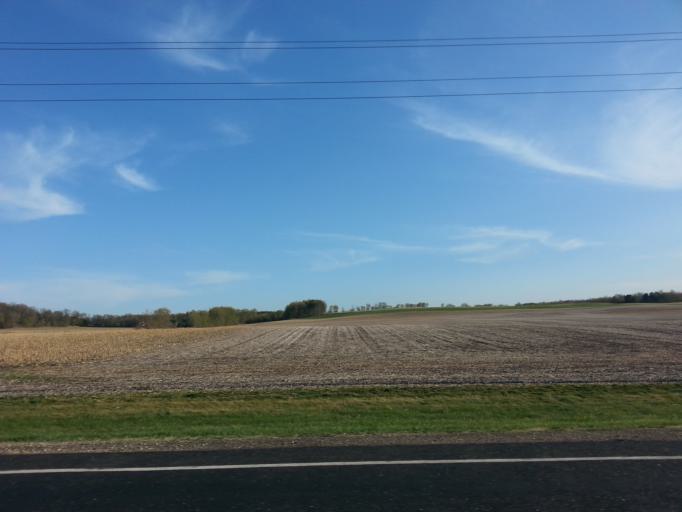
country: US
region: Wisconsin
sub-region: Pierce County
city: River Falls
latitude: 44.8246
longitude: -92.7067
